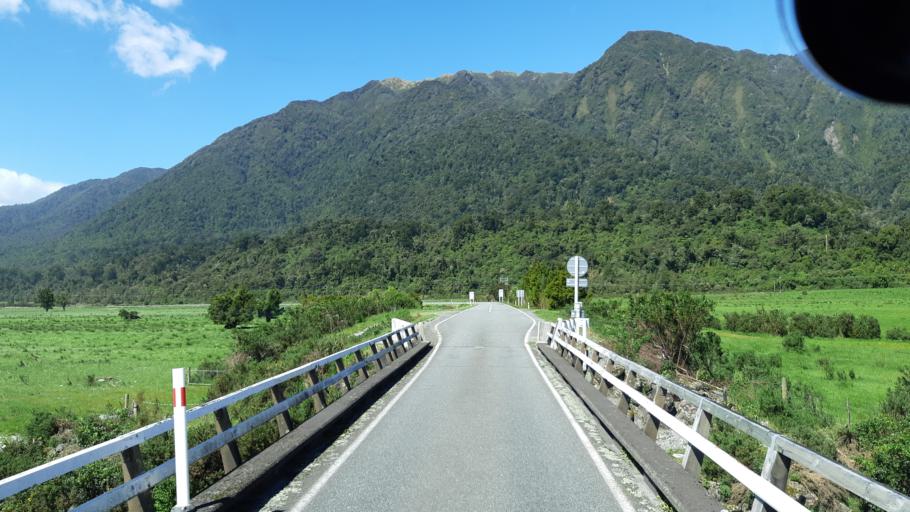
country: NZ
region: West Coast
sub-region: Westland District
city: Hokitika
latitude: -43.1554
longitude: 170.6249
